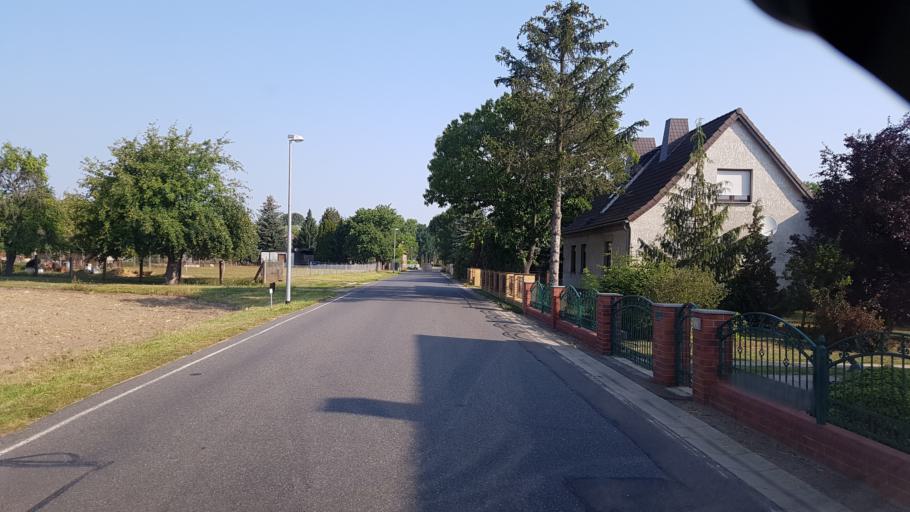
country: DE
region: Brandenburg
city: Drebkau
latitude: 51.6689
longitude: 14.2336
